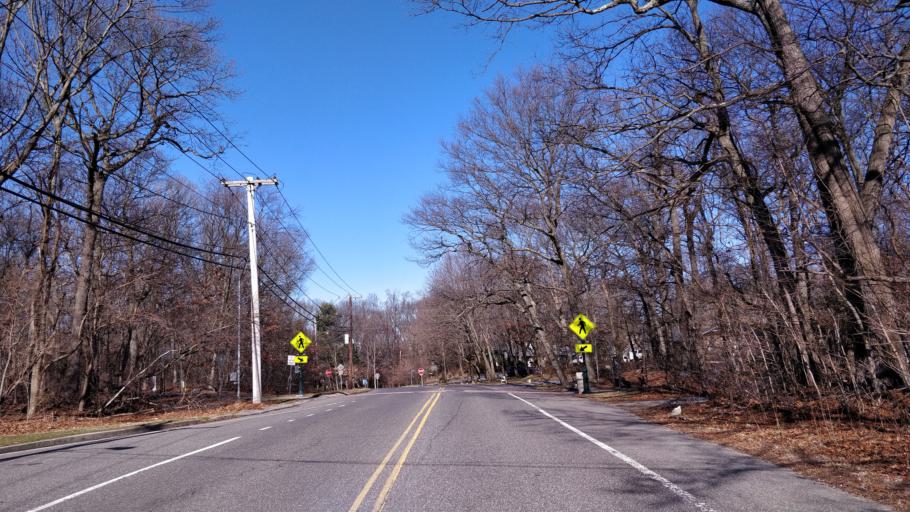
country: US
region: New York
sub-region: Suffolk County
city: Setauket-East Setauket
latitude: 40.9277
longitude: -73.0949
